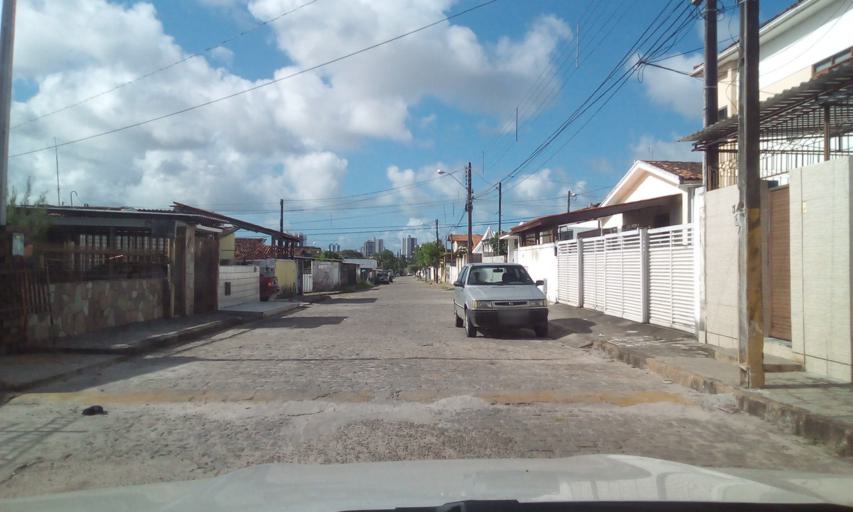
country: BR
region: Paraiba
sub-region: Joao Pessoa
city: Joao Pessoa
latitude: -7.1349
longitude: -34.8533
